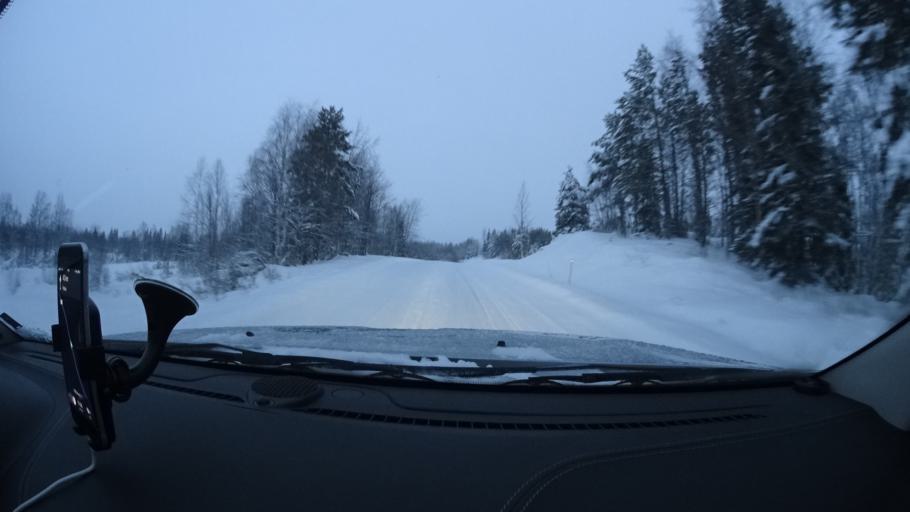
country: FI
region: Lapland
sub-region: Tunturi-Lappi
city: Kittilae
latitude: 67.9215
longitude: 25.0583
